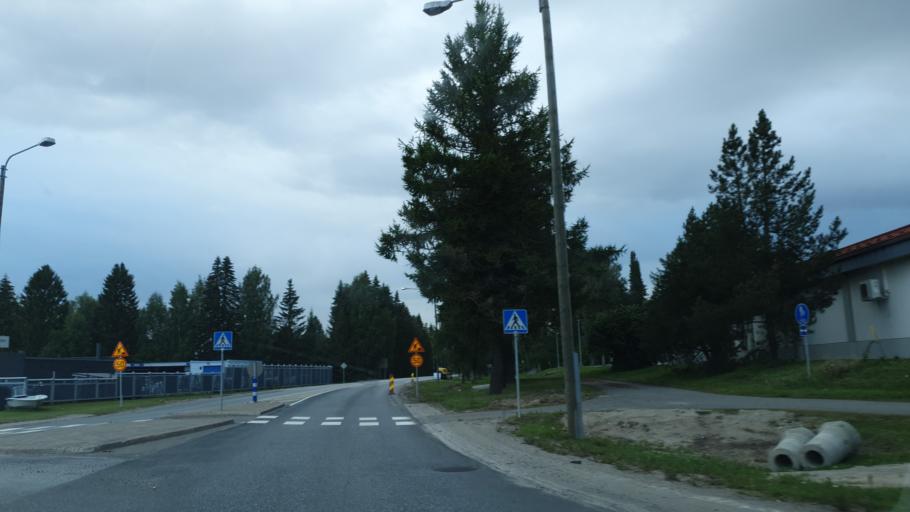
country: FI
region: North Karelia
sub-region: Pielisen Karjala
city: Lieksa
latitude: 63.3168
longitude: 30.0248
